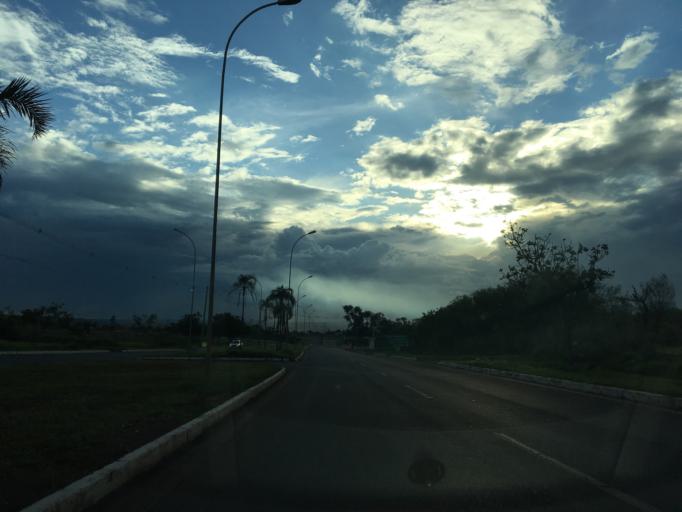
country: BR
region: Federal District
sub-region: Brasilia
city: Brasilia
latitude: -15.8096
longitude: -47.8424
